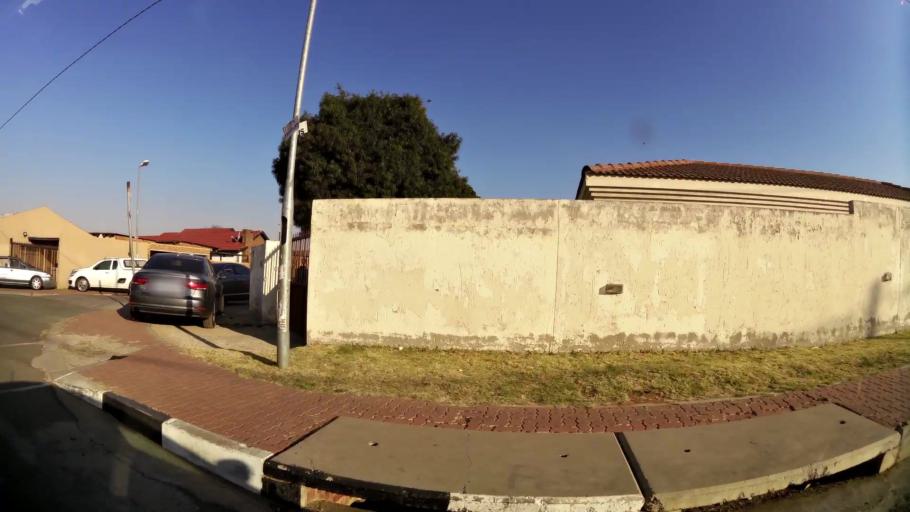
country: ZA
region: Gauteng
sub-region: City of Johannesburg Metropolitan Municipality
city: Soweto
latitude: -26.2596
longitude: 27.8843
